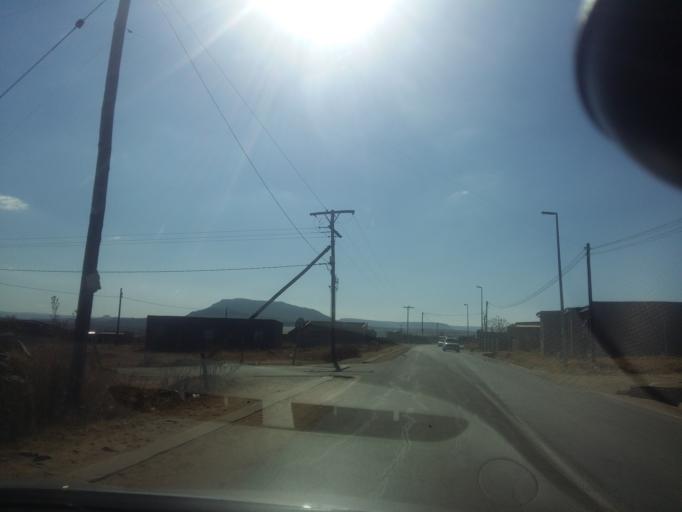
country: LS
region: Maseru
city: Maseru
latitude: -29.3431
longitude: 27.4400
